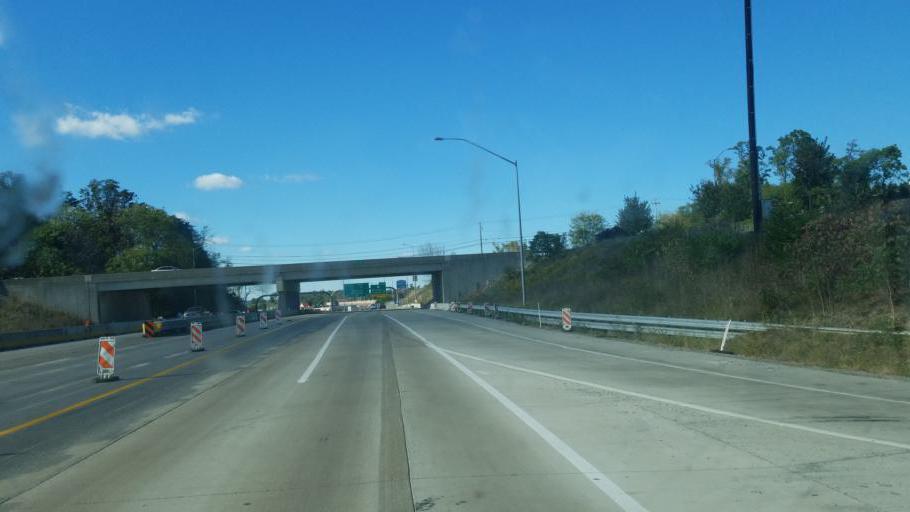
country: US
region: Pennsylvania
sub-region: Washington County
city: East Washington
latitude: 40.1791
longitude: -80.2232
